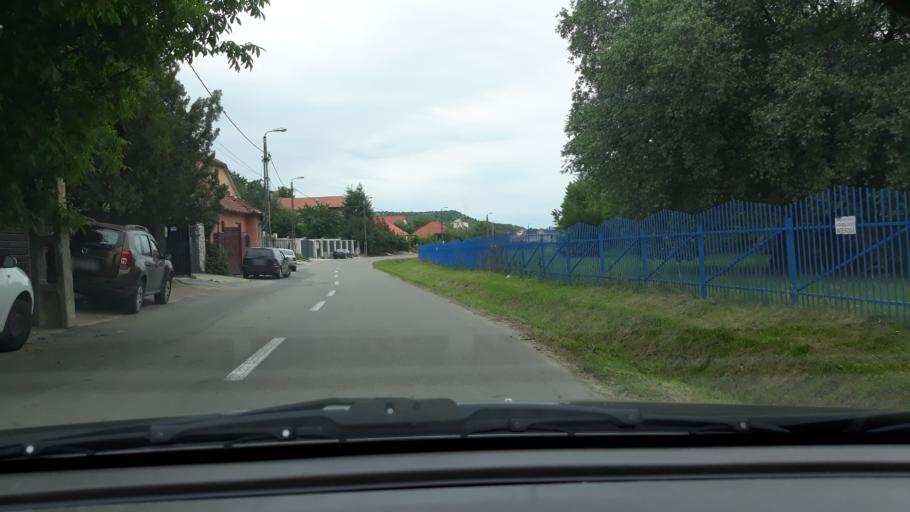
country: RO
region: Bihor
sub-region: Comuna Sanmartin
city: Sanmartin
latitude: 47.0509
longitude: 21.9911
